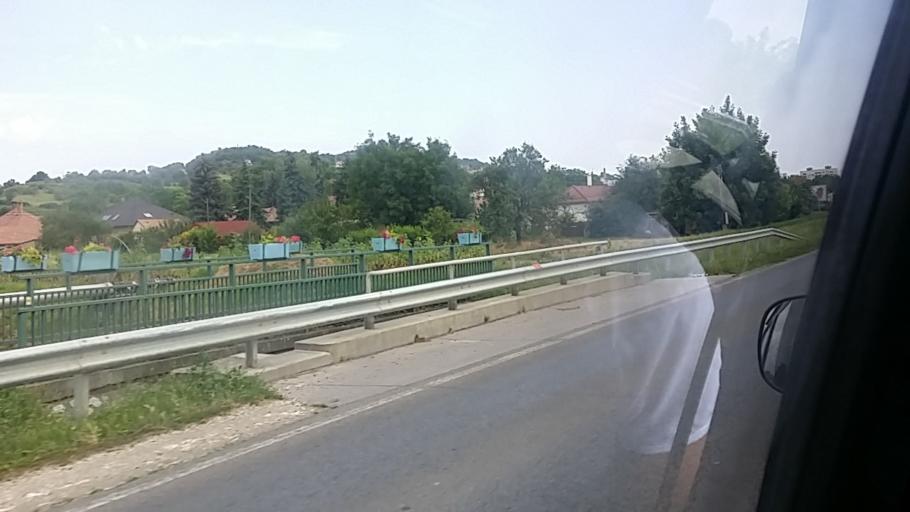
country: HU
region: Tolna
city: Szekszard
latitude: 46.3256
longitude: 18.6983
